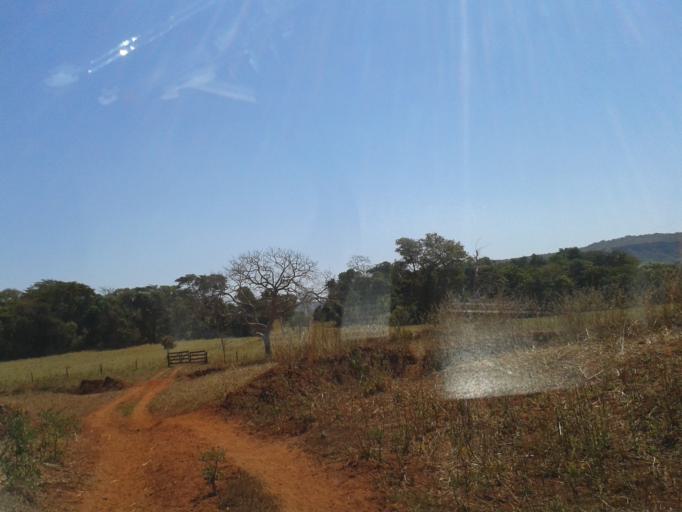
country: BR
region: Minas Gerais
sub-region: Santa Vitoria
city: Santa Vitoria
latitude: -19.0764
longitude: -50.0332
